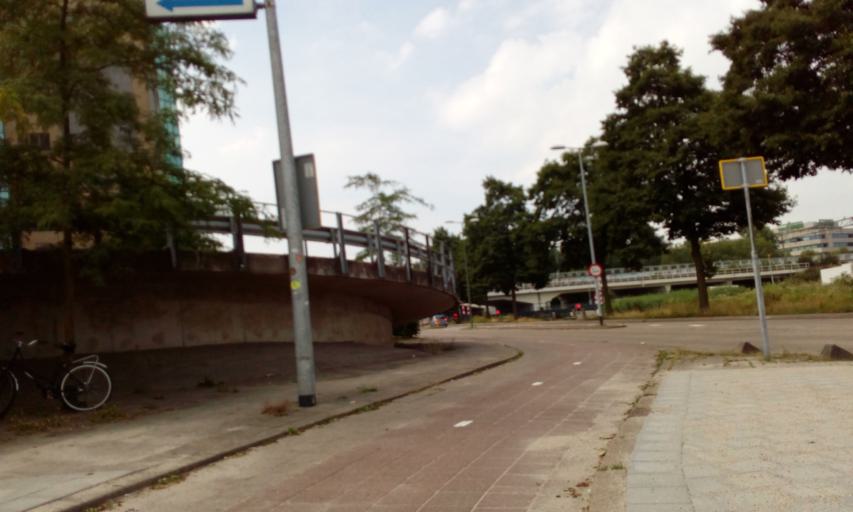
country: NL
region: South Holland
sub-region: Gemeente Schiedam
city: Schiedam
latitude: 51.9237
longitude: 4.4083
